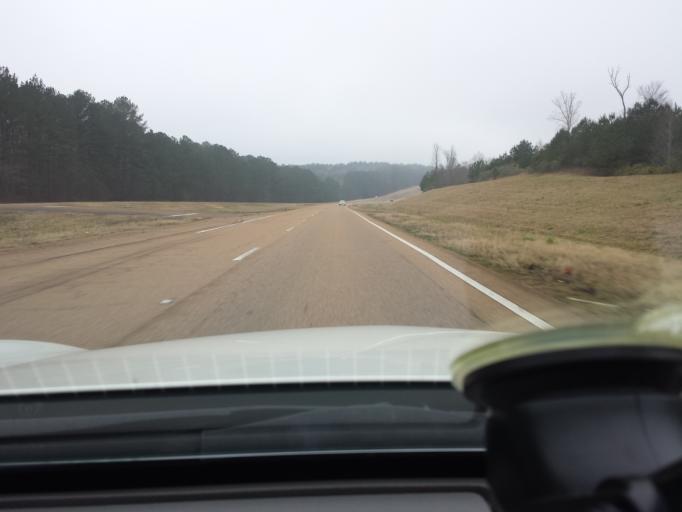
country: US
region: Mississippi
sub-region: Winston County
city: Louisville
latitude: 33.1742
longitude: -89.0225
